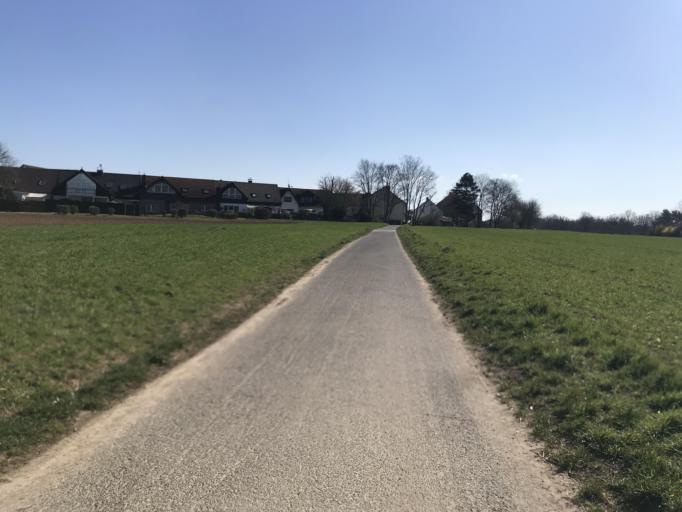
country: DE
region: Hesse
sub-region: Regierungsbezirk Darmstadt
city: Florsheim
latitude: 50.0118
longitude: 8.4127
